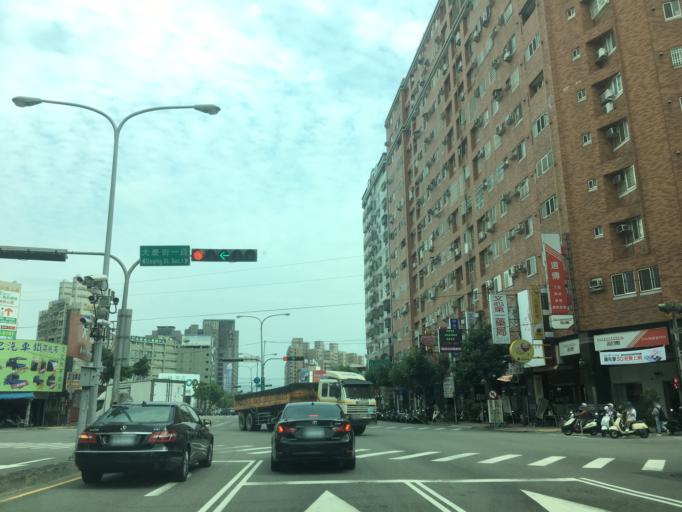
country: TW
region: Taiwan
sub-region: Taichung City
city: Taichung
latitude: 24.1142
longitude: 120.6563
